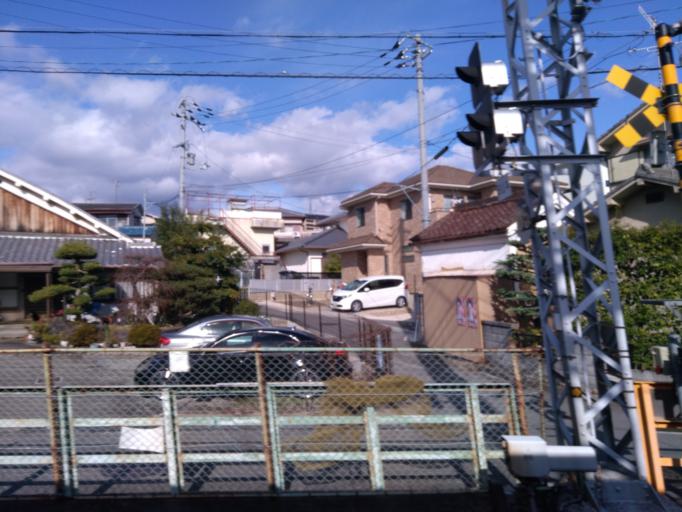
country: JP
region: Hyogo
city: Takarazuka
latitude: 34.8205
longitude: 135.3825
